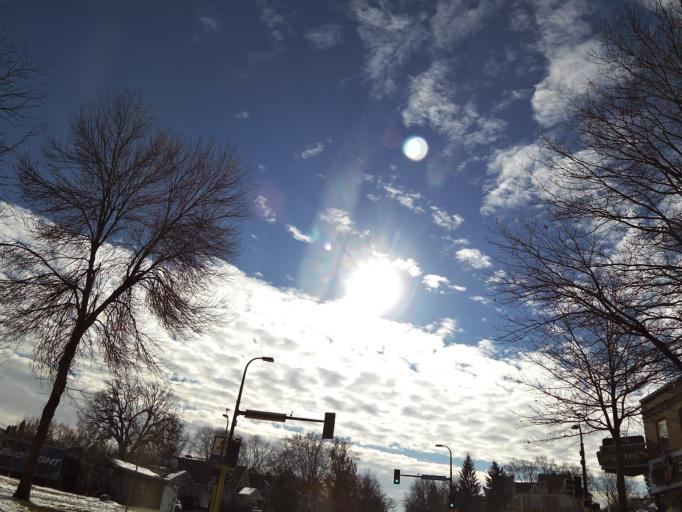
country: US
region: Minnesota
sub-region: Hennepin County
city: Richfield
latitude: 44.9309
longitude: -93.2883
